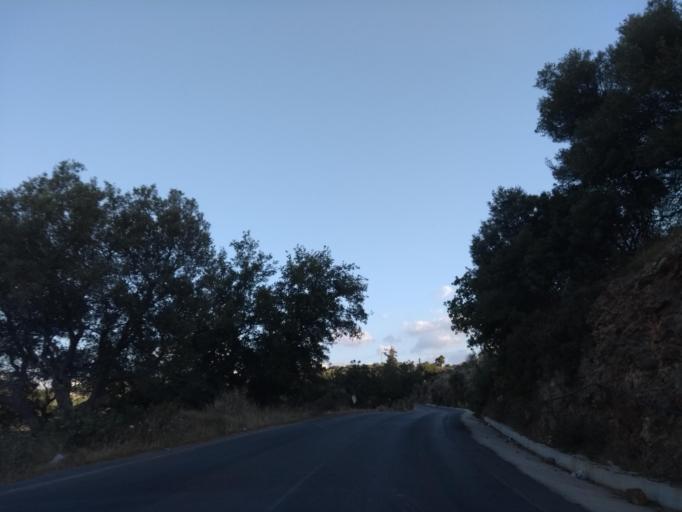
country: GR
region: Crete
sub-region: Nomos Chanias
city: Kalivai
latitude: 35.4230
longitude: 24.1857
